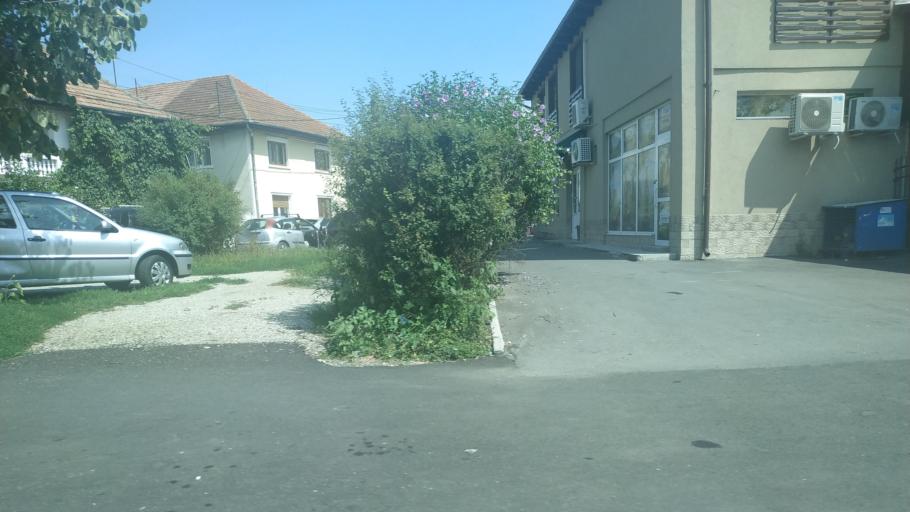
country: RO
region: Brasov
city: Fogarasch
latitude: 45.8386
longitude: 24.9673
